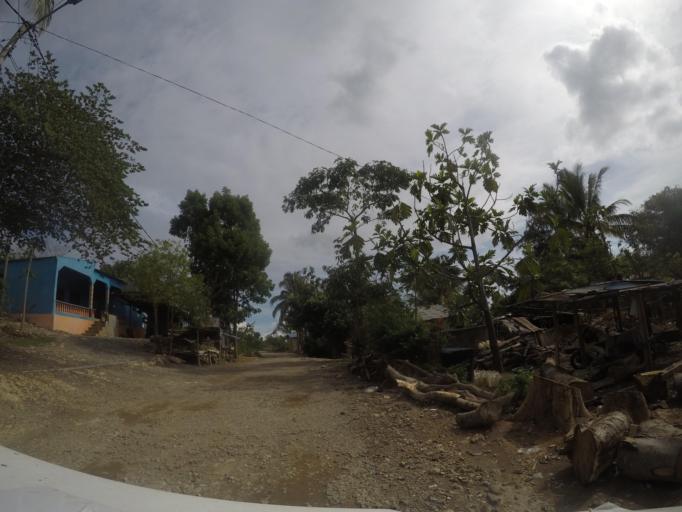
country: TL
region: Baucau
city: Baucau
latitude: -8.4762
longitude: 126.4536
